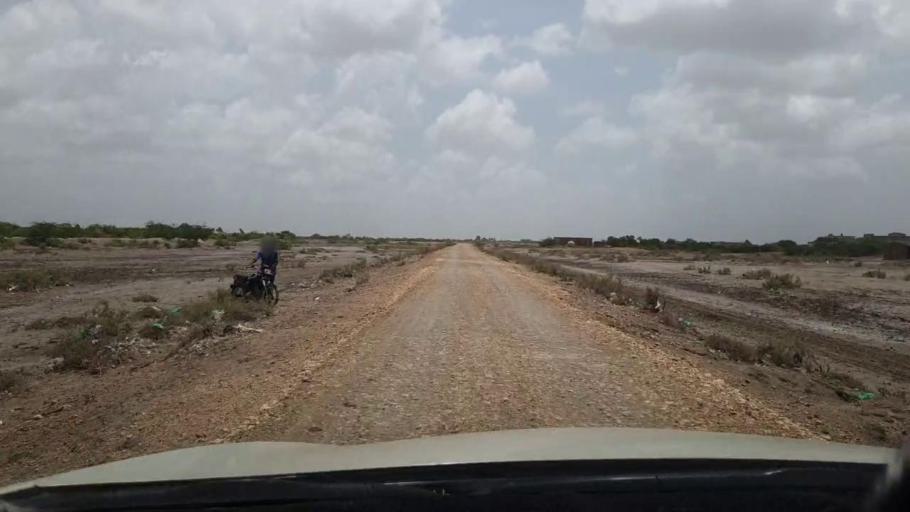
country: PK
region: Sindh
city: Kadhan
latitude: 24.3974
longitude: 68.9362
